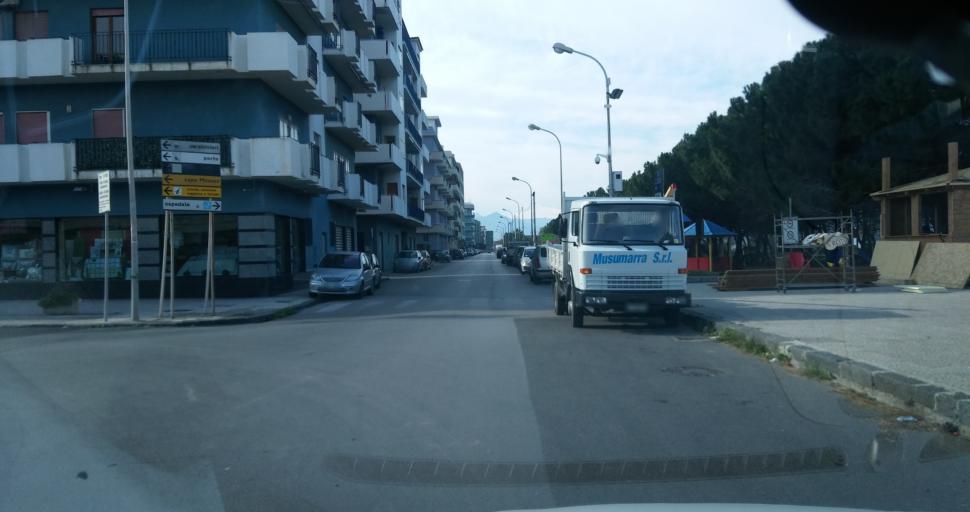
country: IT
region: Sicily
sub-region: Messina
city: Milazzo
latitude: 38.2267
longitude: 15.2364
